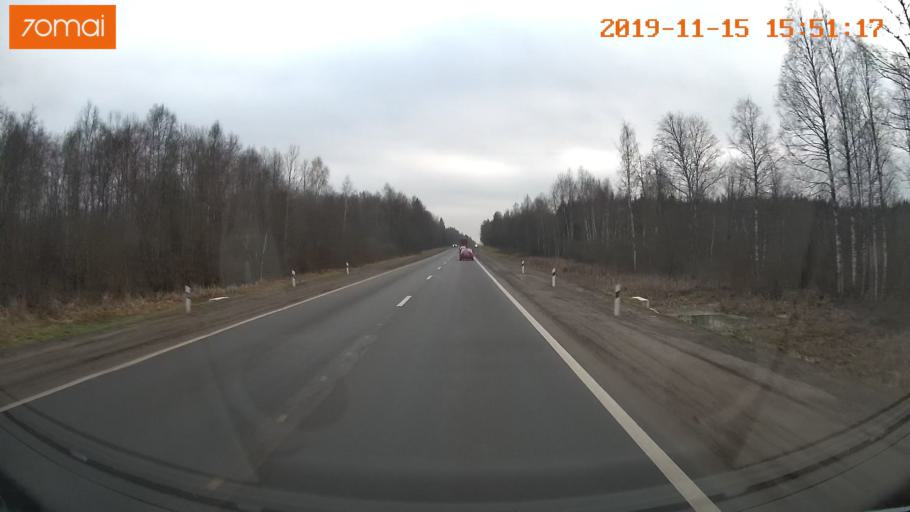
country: RU
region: Jaroslavl
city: Yaroslavl
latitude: 57.8964
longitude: 40.0087
